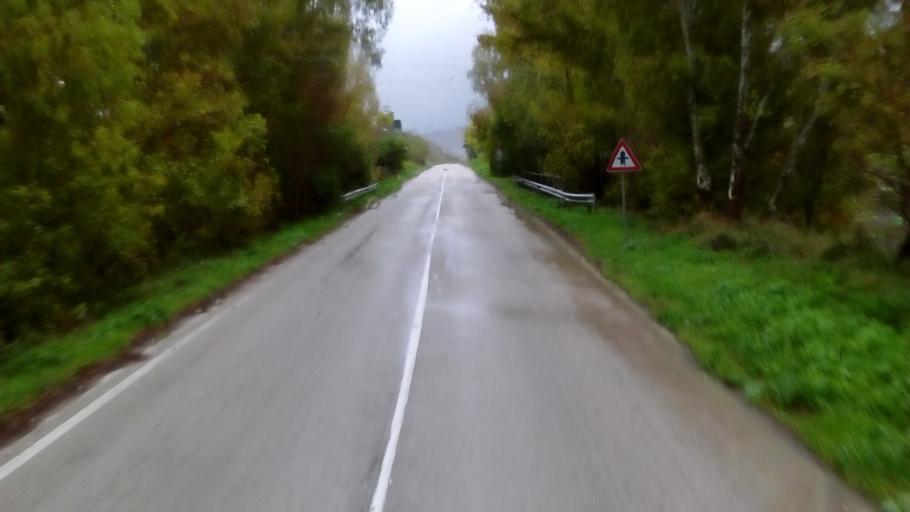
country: IT
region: Sicily
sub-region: Enna
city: Pietraperzia
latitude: 37.4567
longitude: 14.1762
